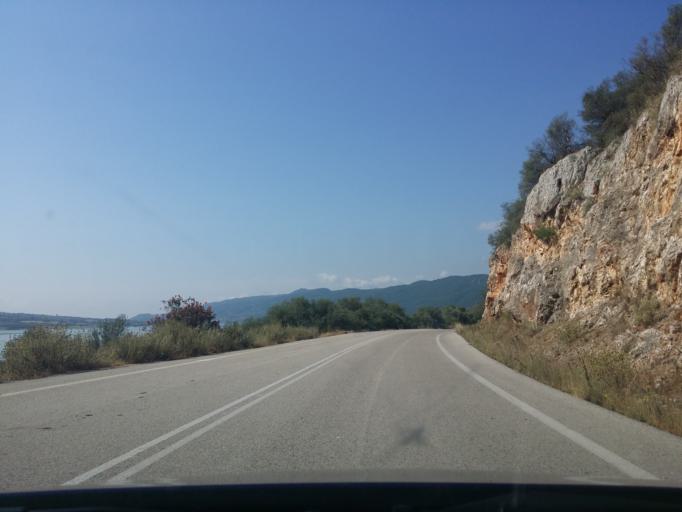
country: GR
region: West Greece
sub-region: Nomos Aitolias kai Akarnanias
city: Stanos
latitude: 38.7769
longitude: 21.1849
